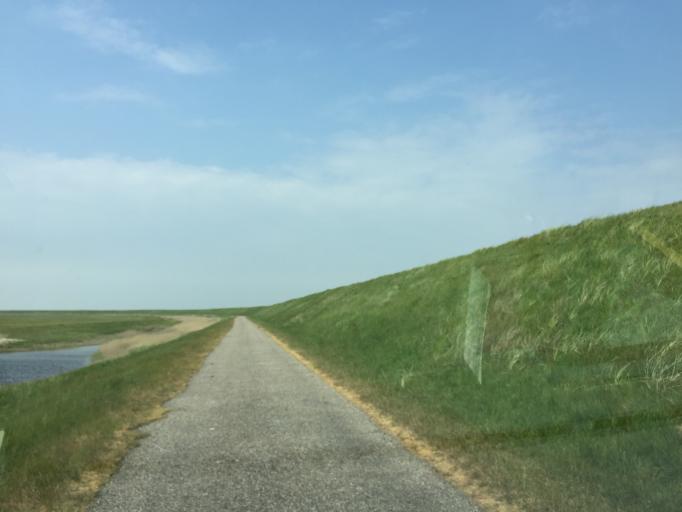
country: DK
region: South Denmark
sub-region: Esbjerg Kommune
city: Tjaereborg
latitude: 55.2916
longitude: 8.5690
